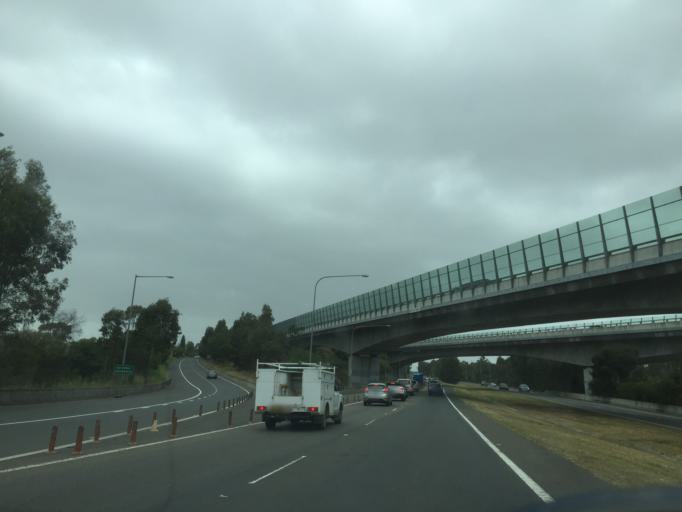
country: AU
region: New South Wales
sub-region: Blacktown
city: Blacktown
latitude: -33.7523
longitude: 150.9521
